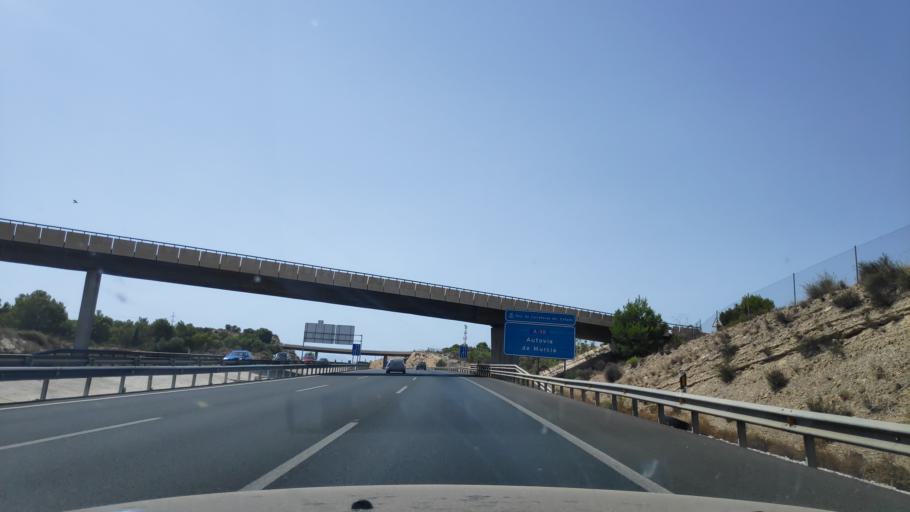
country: ES
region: Murcia
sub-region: Murcia
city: Molina de Segura
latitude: 38.0446
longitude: -1.1651
